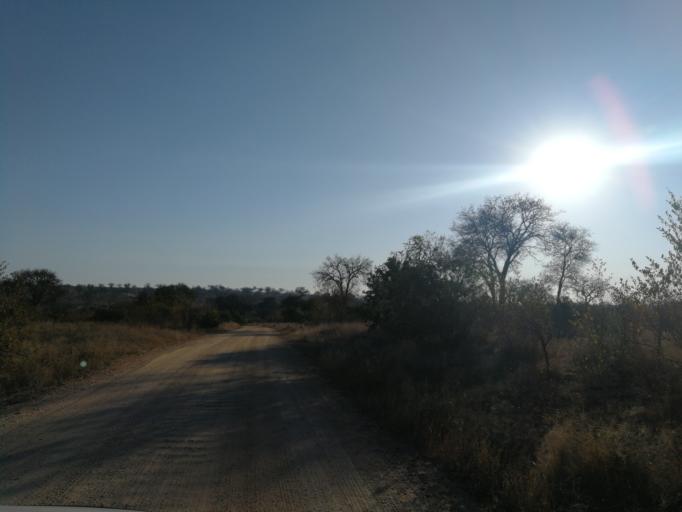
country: ZA
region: Limpopo
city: Thulamahashi
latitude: -25.0133
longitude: 31.4290
